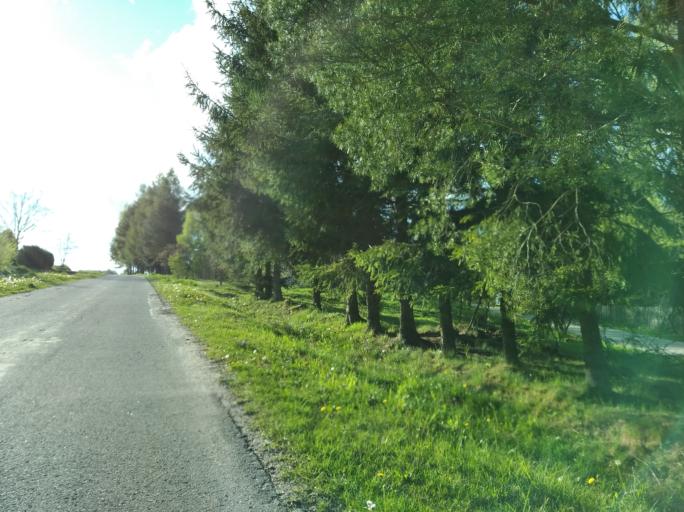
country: PL
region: Subcarpathian Voivodeship
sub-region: Powiat strzyzowski
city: Wysoka Strzyzowska
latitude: 49.7997
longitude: 21.7973
